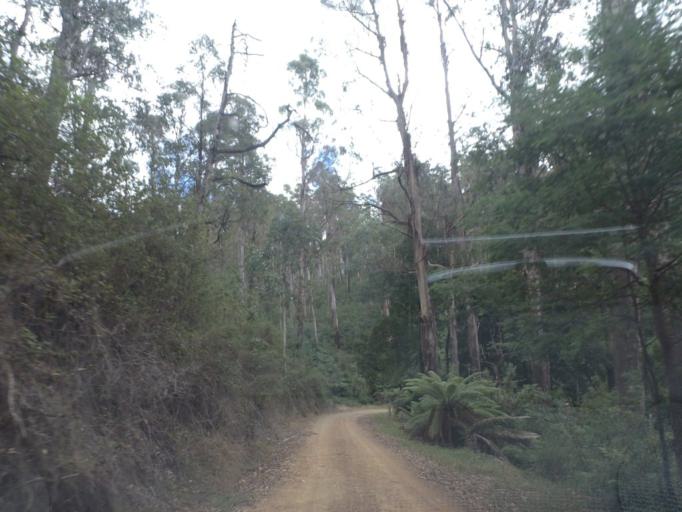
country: AU
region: Victoria
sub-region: Murrindindi
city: Alexandra
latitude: -37.4331
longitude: 145.9658
